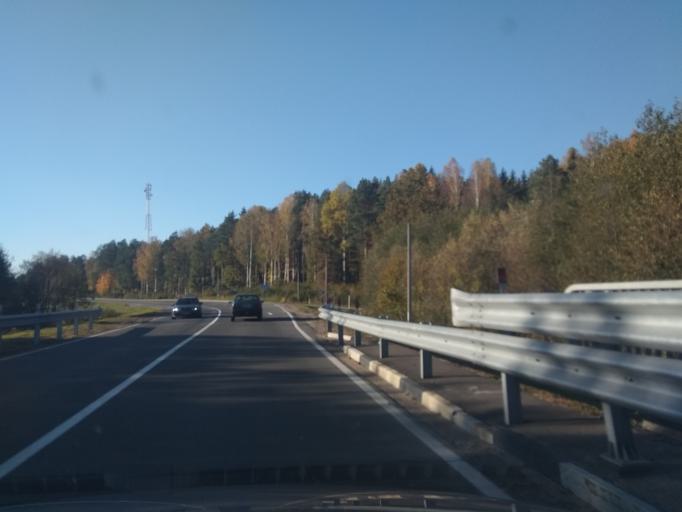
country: BY
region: Grodnenskaya
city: Vyalikaya Byerastavitsa
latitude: 53.1198
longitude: 23.9201
